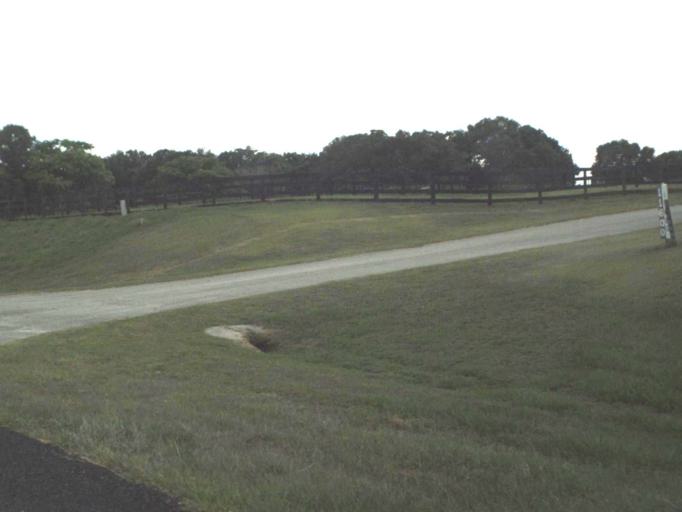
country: US
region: Florida
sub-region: Marion County
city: Citra
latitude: 29.3183
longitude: -82.1519
